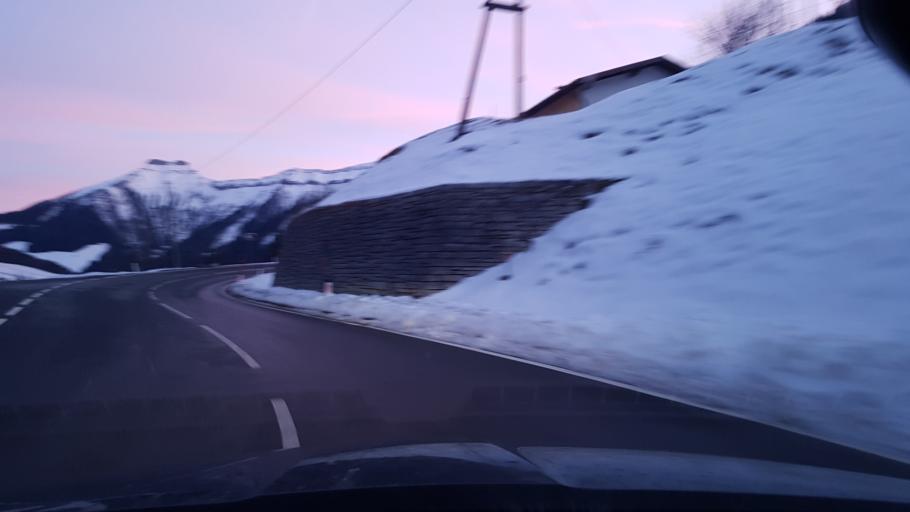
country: AT
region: Salzburg
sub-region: Politischer Bezirk Hallein
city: Krispl
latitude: 47.7153
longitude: 13.1863
